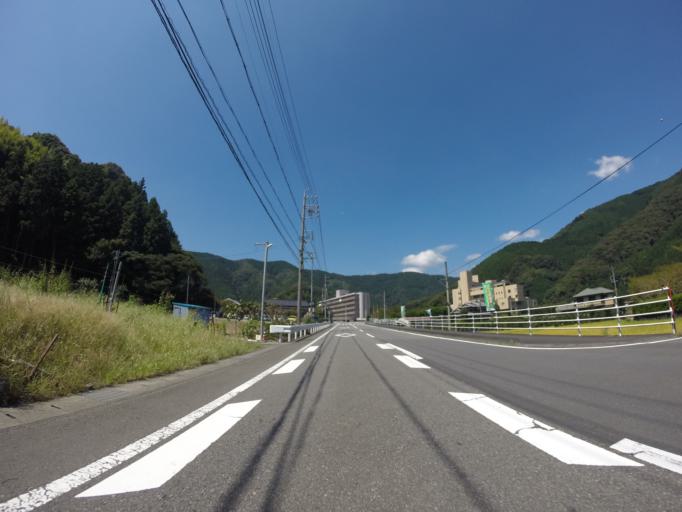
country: JP
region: Shizuoka
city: Shizuoka-shi
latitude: 35.0196
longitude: 138.2618
